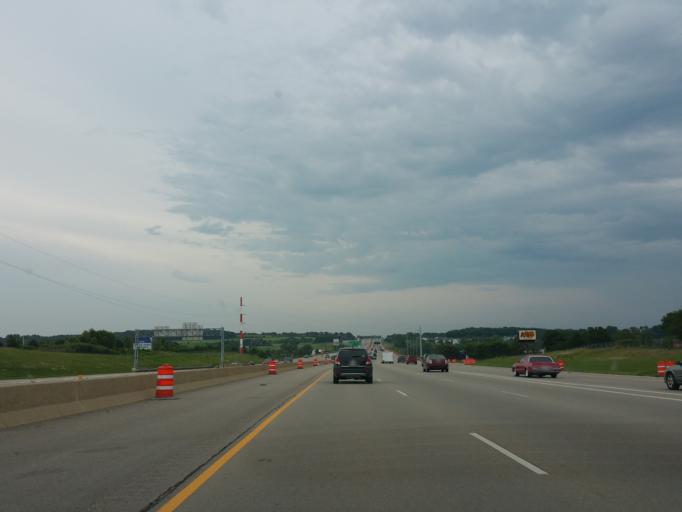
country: US
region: Wisconsin
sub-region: Dane County
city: Monona
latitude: 43.1323
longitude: -89.2932
